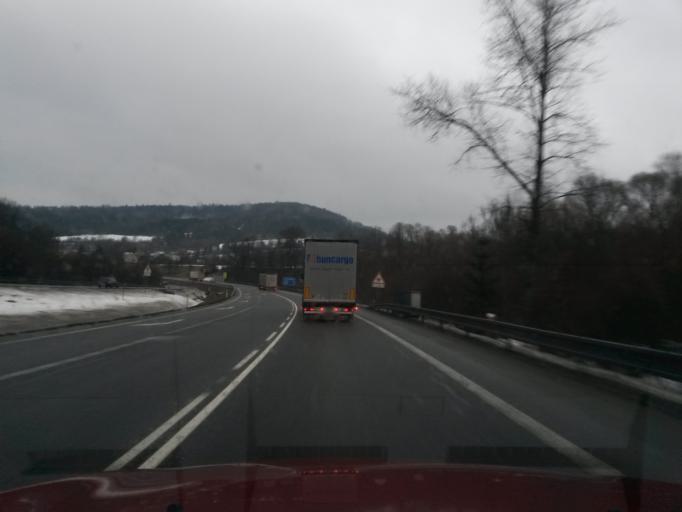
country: SK
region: Zilinsky
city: Cadca
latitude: 49.4224
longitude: 18.8371
